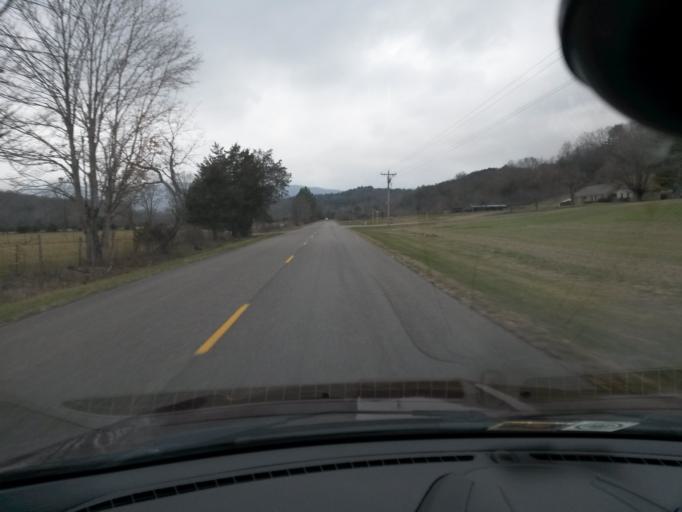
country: US
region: Virginia
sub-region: City of Lexington
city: Lexington
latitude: 37.8619
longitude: -79.5143
